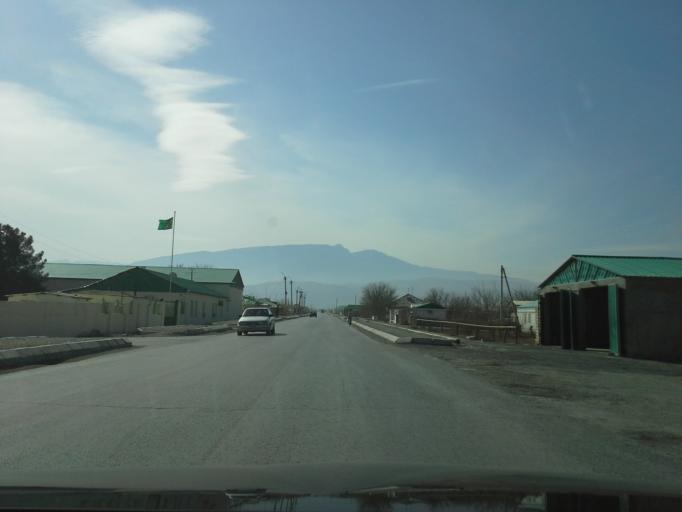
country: TM
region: Ahal
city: Abadan
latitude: 38.1127
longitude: 58.0348
